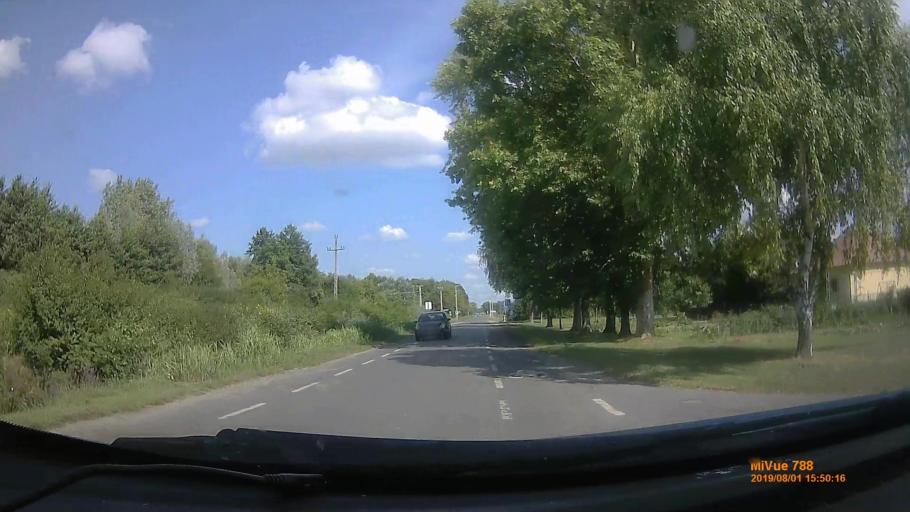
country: HU
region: Baranya
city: Szentlorinc
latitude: 46.0376
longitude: 17.9979
